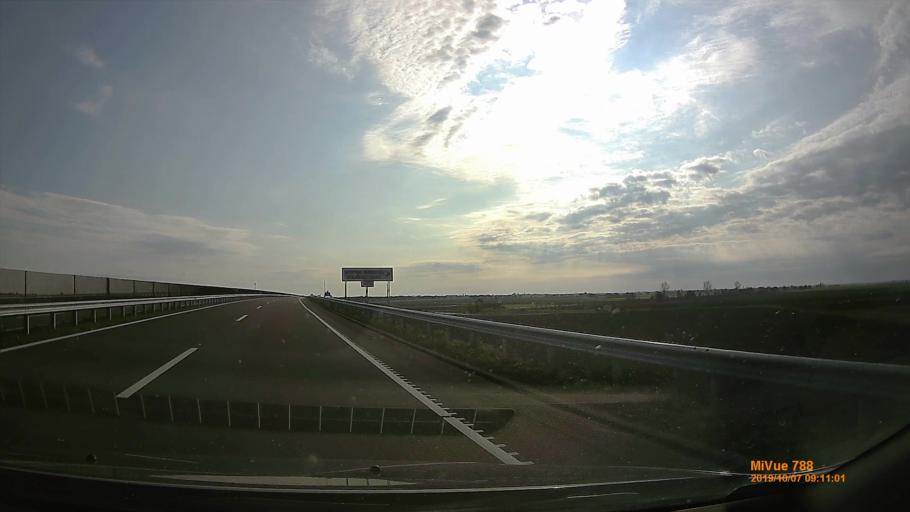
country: HU
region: Bekes
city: Nagyszenas
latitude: 46.8125
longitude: 20.6691
